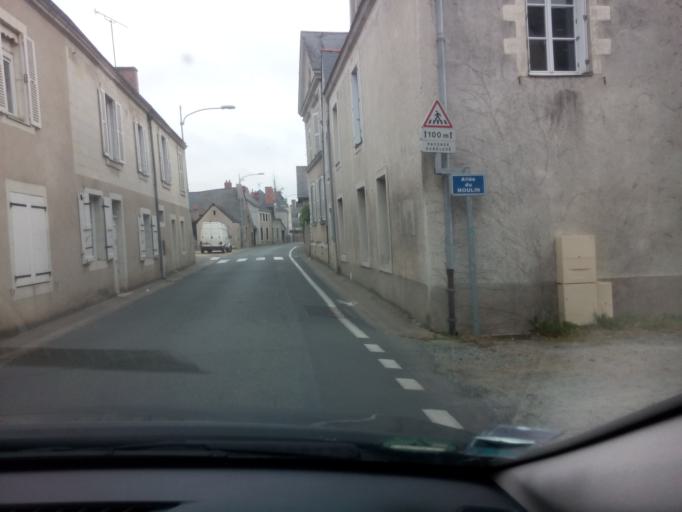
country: FR
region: Pays de la Loire
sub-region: Departement de Maine-et-Loire
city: Tierce
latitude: 47.6214
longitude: -0.5066
